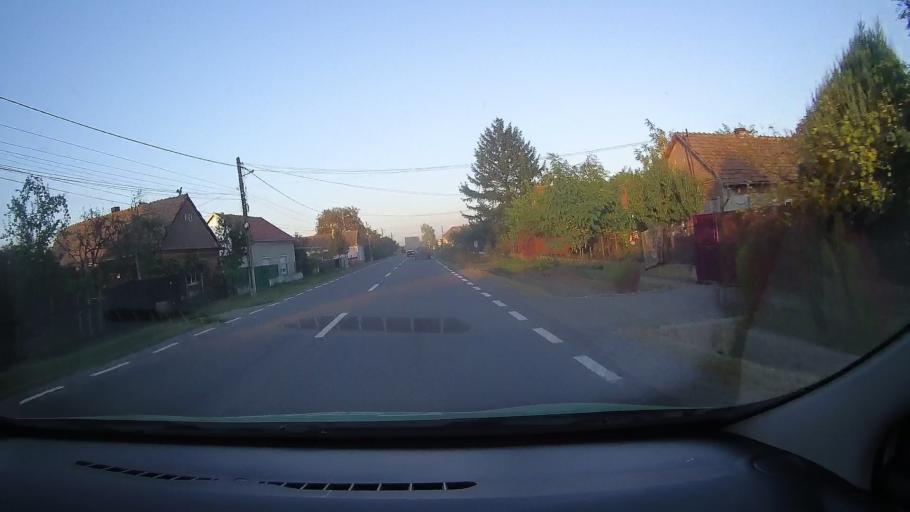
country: RO
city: Dioszeg
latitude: 47.2856
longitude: 21.9929
